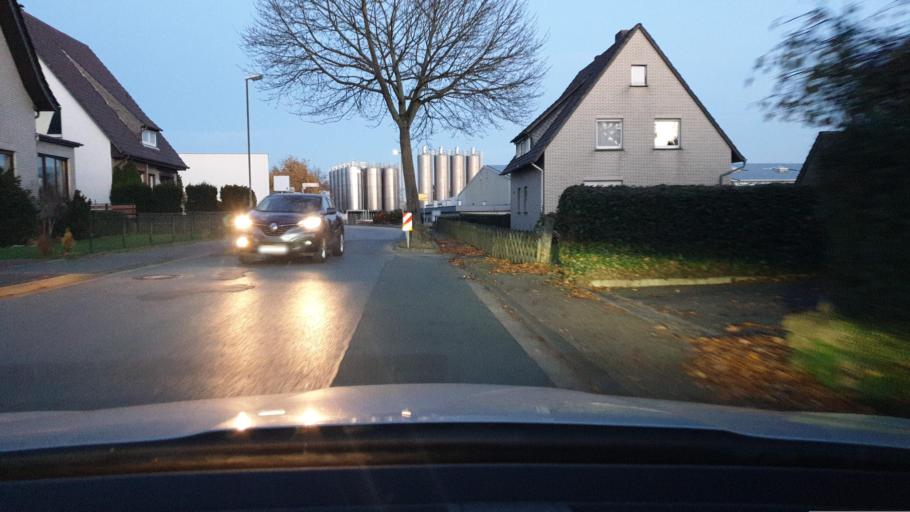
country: DE
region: North Rhine-Westphalia
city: Bad Oeynhausen
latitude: 52.2115
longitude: 8.7672
